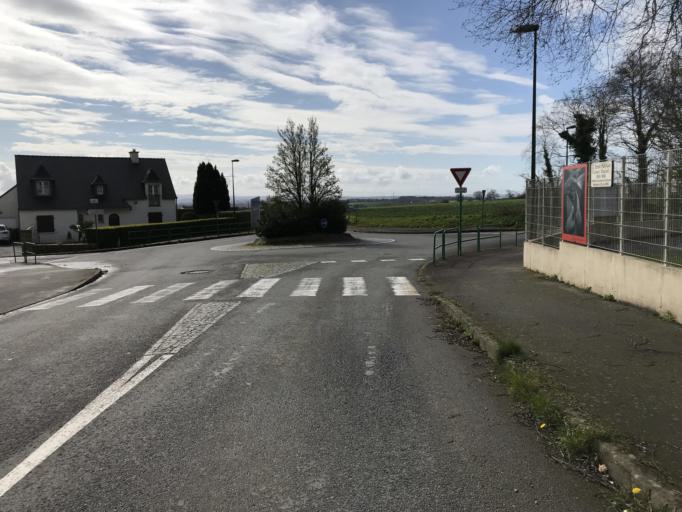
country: FR
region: Brittany
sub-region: Departement du Finistere
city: Dirinon
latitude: 48.3968
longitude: -4.2648
